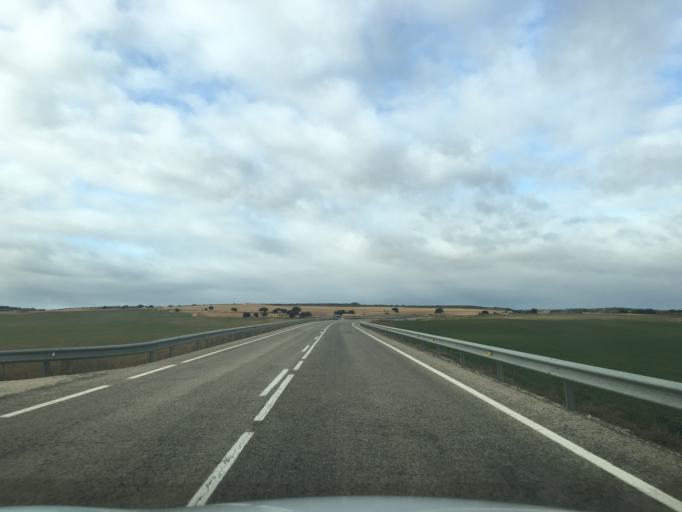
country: ES
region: Castille-La Mancha
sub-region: Provincia de Albacete
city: Petrola
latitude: 38.8243
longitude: -1.5829
